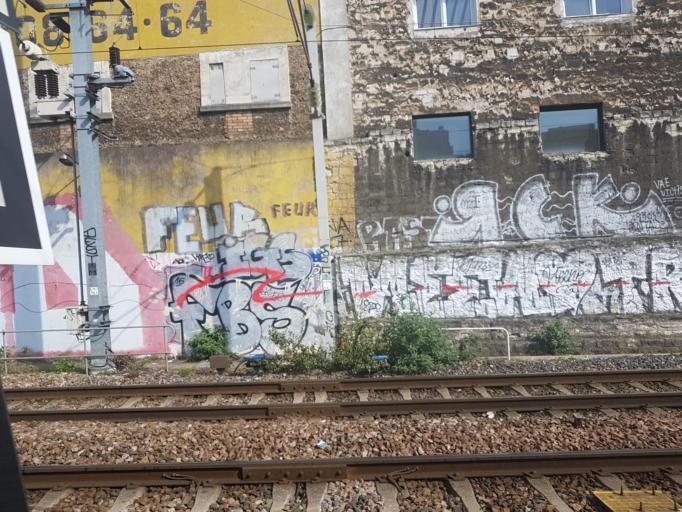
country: FR
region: Ile-de-France
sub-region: Paris
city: Saint-Ouen
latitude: 48.8853
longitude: 2.3639
